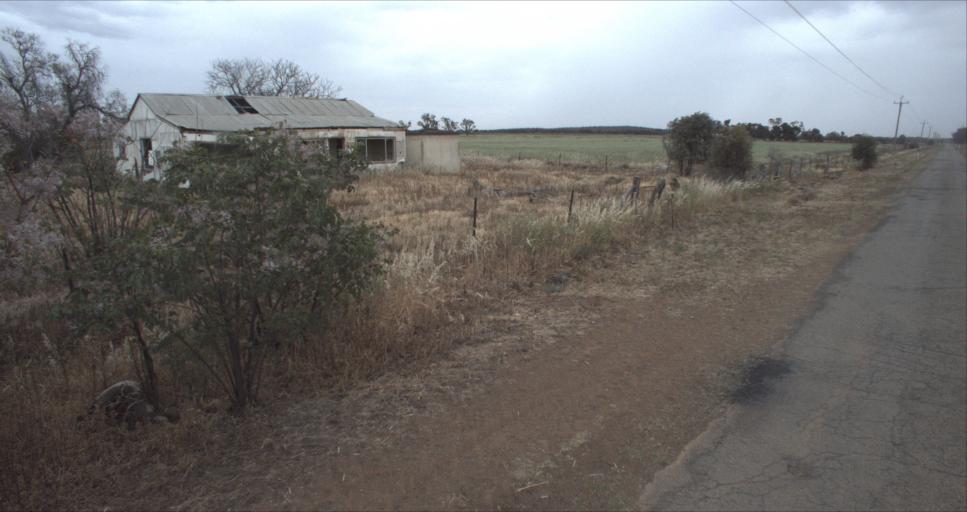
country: AU
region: New South Wales
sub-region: Leeton
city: Leeton
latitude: -34.4124
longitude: 146.3401
